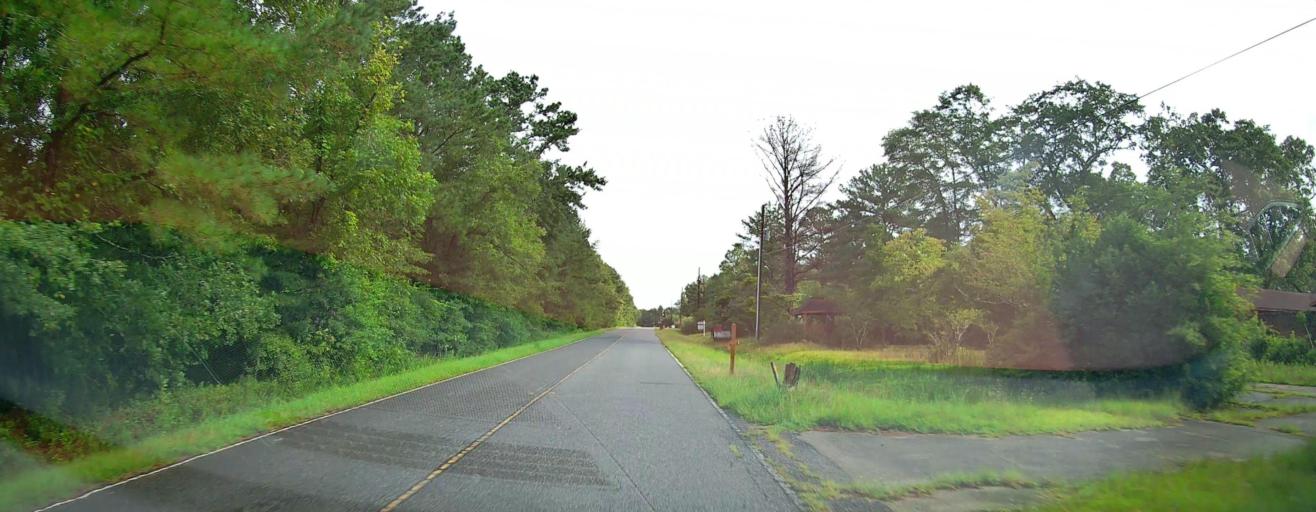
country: US
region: Georgia
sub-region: Bibb County
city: West Point
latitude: 32.8024
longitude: -83.7839
